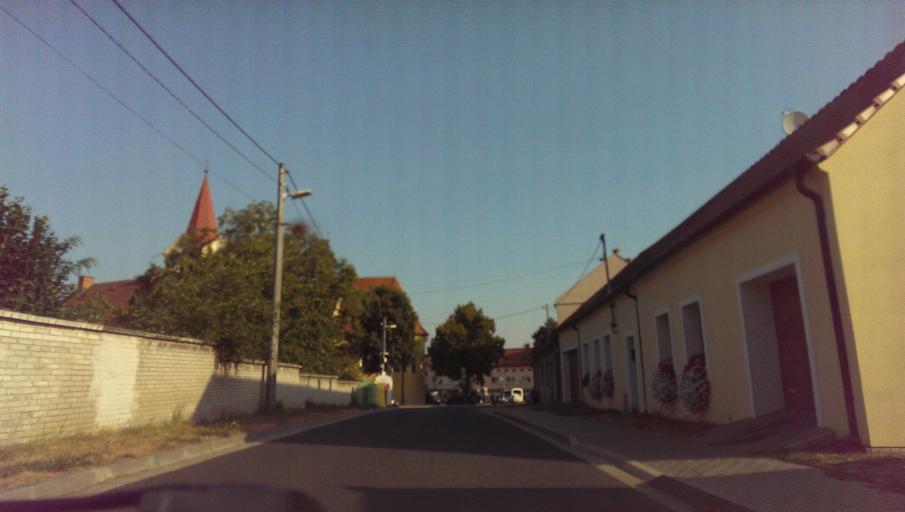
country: CZ
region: Zlin
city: Korycany
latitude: 49.1052
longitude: 17.1645
